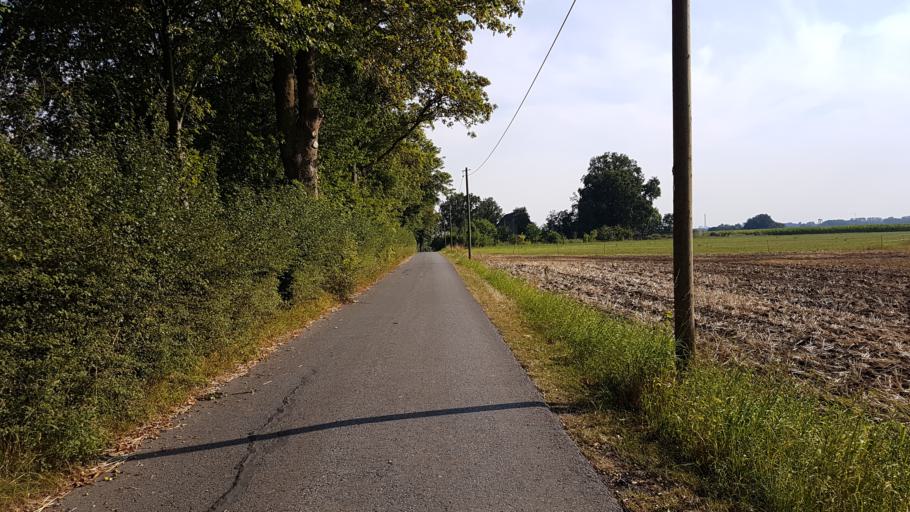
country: DE
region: North Rhine-Westphalia
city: Olfen
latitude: 51.6882
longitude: 7.3769
